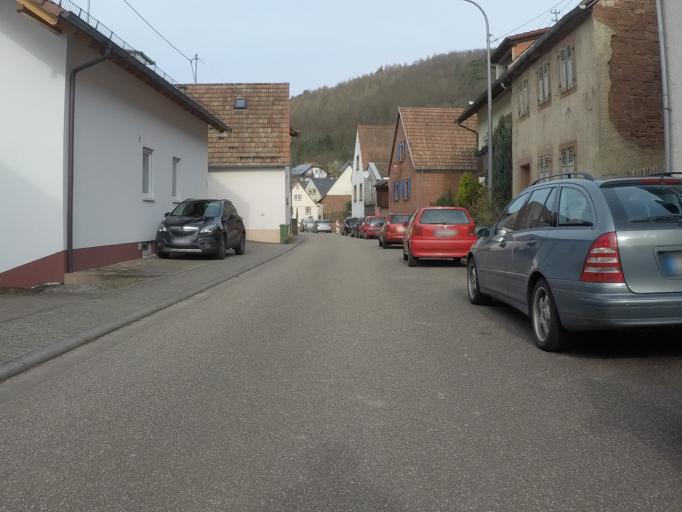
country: DE
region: Rheinland-Pfalz
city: Waldrohrbach
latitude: 49.1699
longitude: 7.9678
